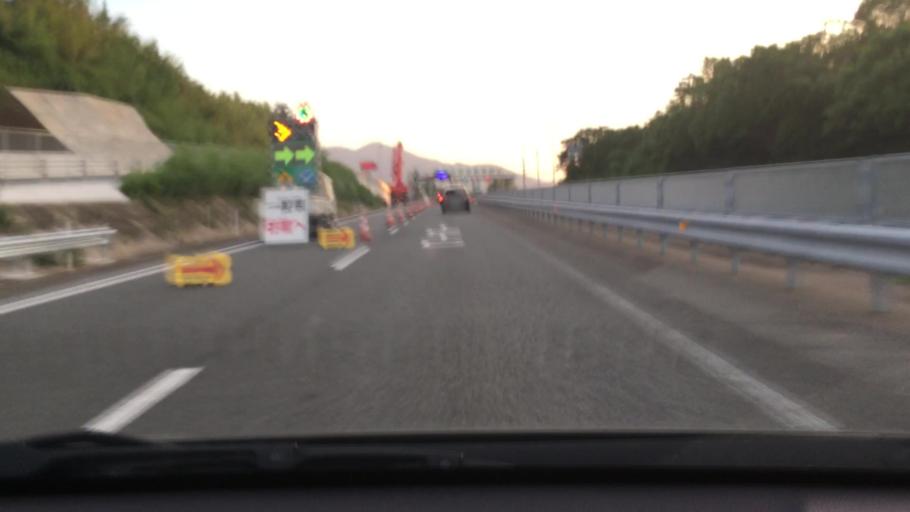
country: JP
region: Fukuoka
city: Maebaru-chuo
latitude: 33.5434
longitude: 130.2038
